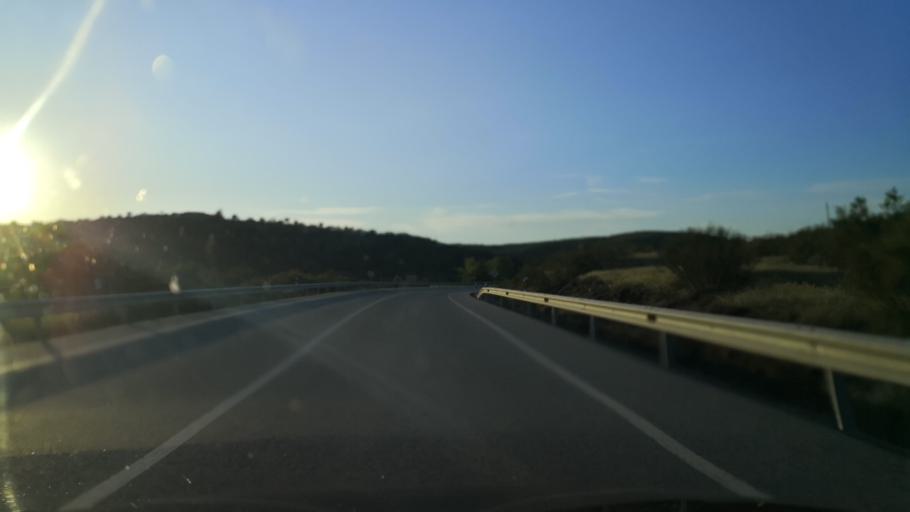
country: ES
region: Extremadura
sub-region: Provincia de Caceres
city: Valencia de Alcantara
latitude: 39.4712
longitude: -7.2097
